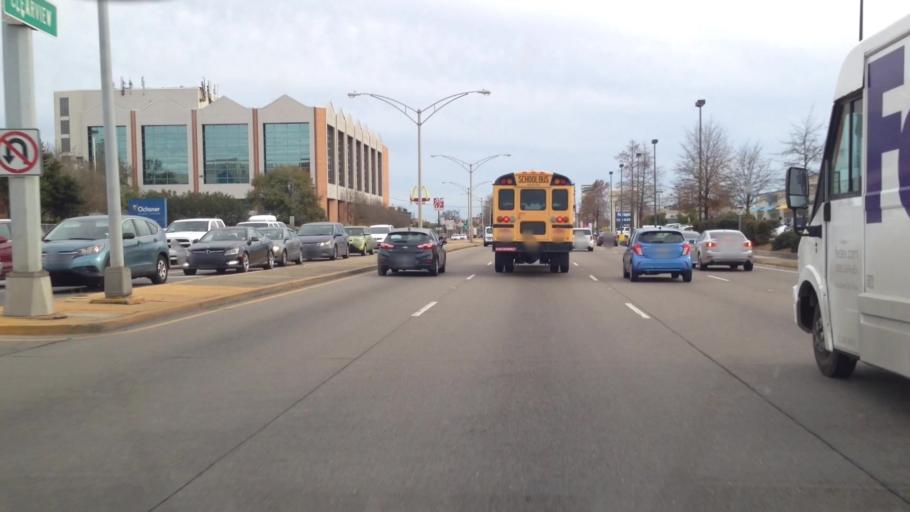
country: US
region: Louisiana
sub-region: Jefferson Parish
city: Elmwood
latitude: 29.9640
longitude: -90.1853
